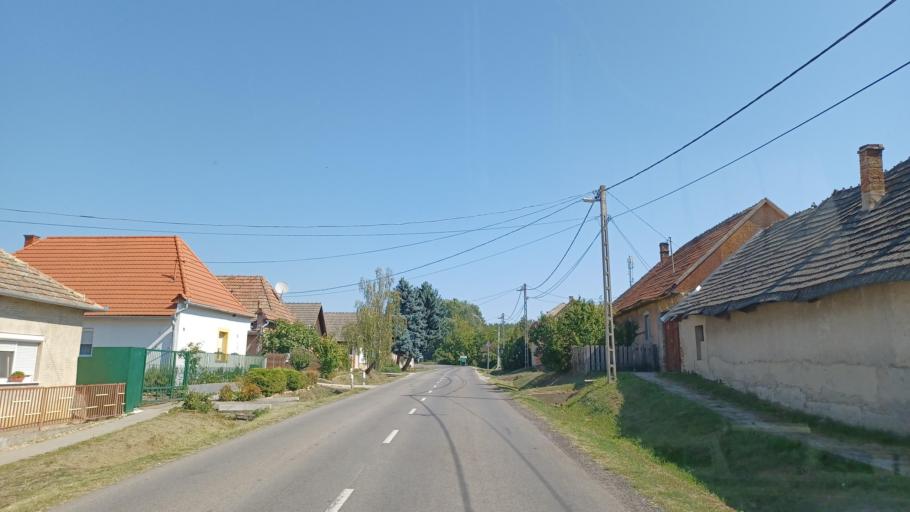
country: HU
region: Tolna
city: Nagydorog
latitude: 46.6793
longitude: 18.6663
